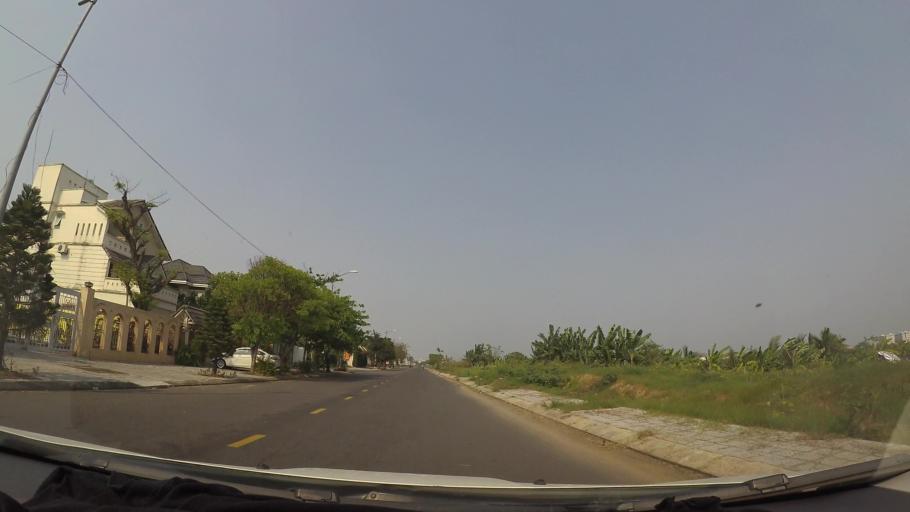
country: VN
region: Da Nang
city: Cam Le
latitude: 16.0037
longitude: 108.1968
